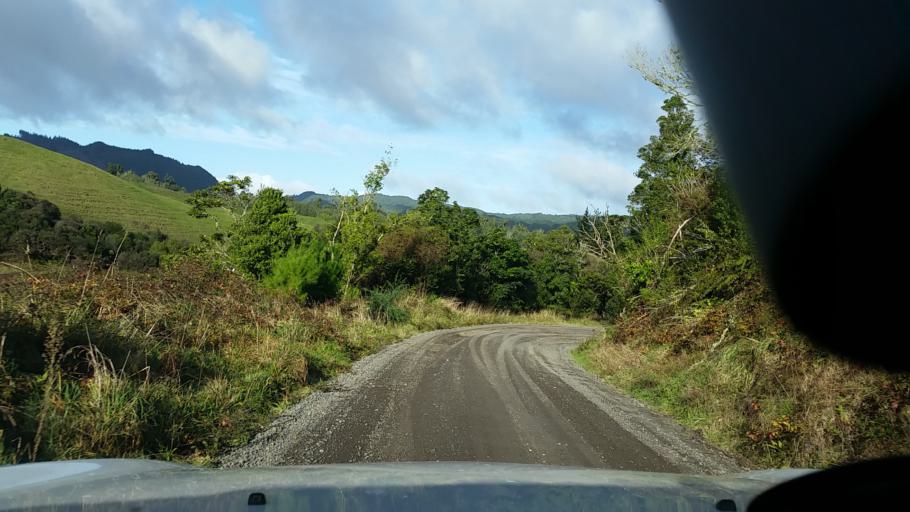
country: NZ
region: Bay of Plenty
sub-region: Kawerau District
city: Kawerau
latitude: -38.0358
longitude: 176.5512
